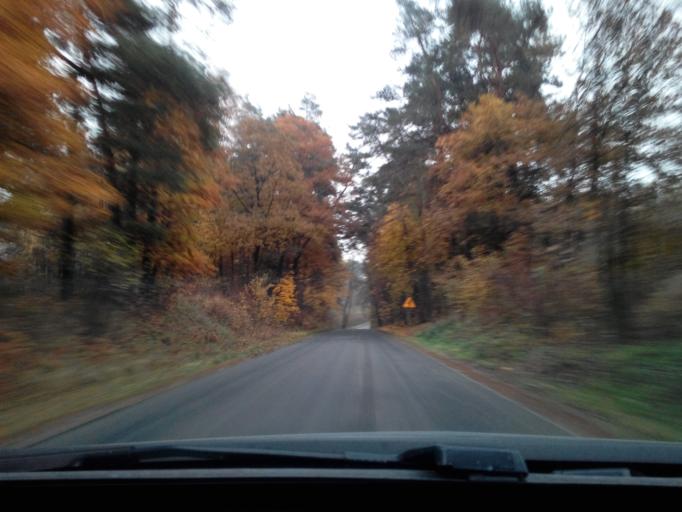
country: PL
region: Kujawsko-Pomorskie
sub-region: Powiat brodnicki
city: Bartniczka
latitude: 53.2485
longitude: 19.5921
